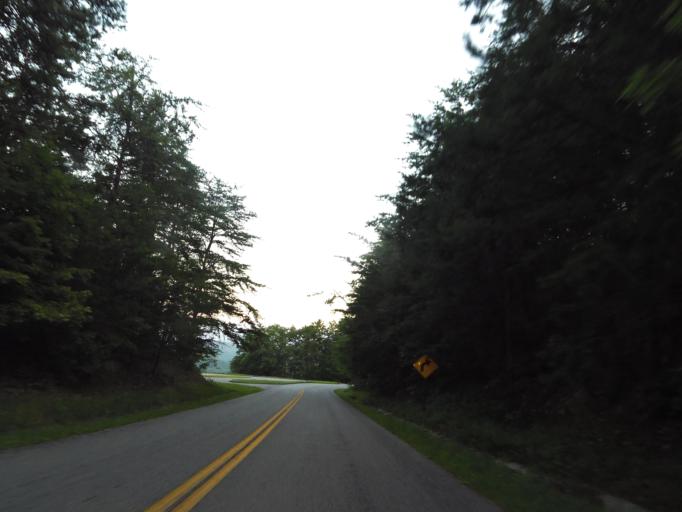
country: US
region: Tennessee
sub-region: Blount County
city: Maryville
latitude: 35.6052
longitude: -83.9814
